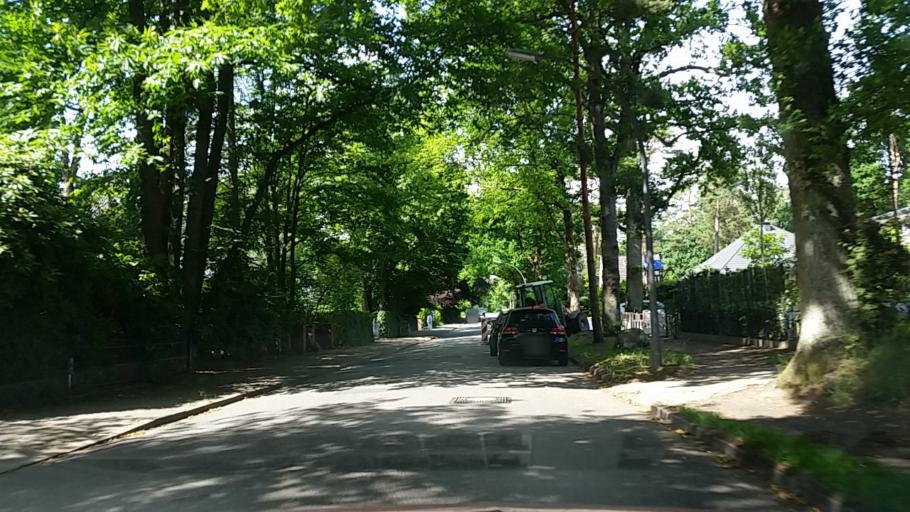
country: DE
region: Schleswig-Holstein
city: Wedel
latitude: 53.5852
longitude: 9.7641
